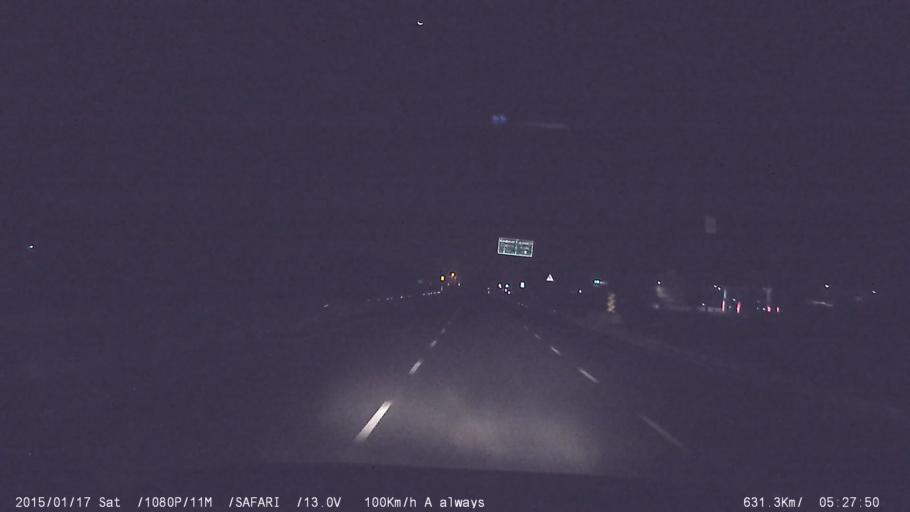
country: IN
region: Tamil Nadu
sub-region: Vellore
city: Arcot
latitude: 12.9280
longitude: 79.2636
